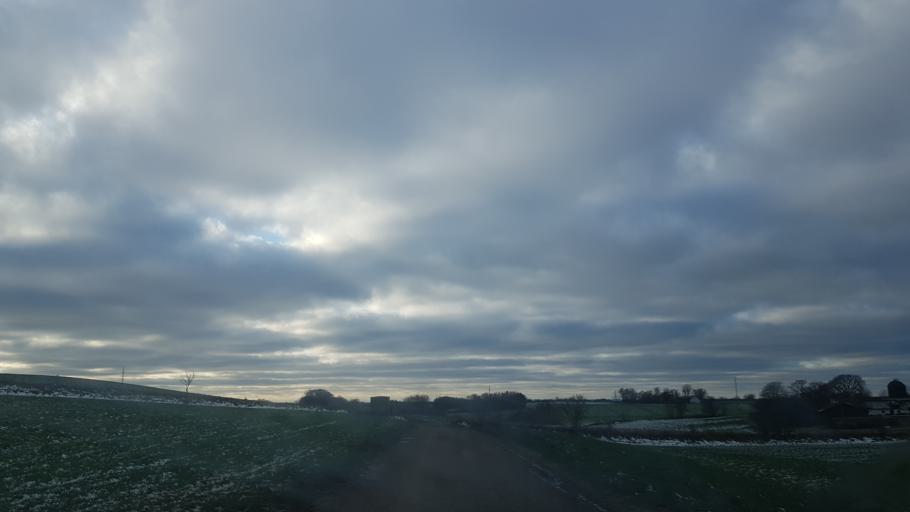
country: DK
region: Zealand
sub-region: Odsherred Kommune
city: Hojby
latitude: 55.9242
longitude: 11.5751
